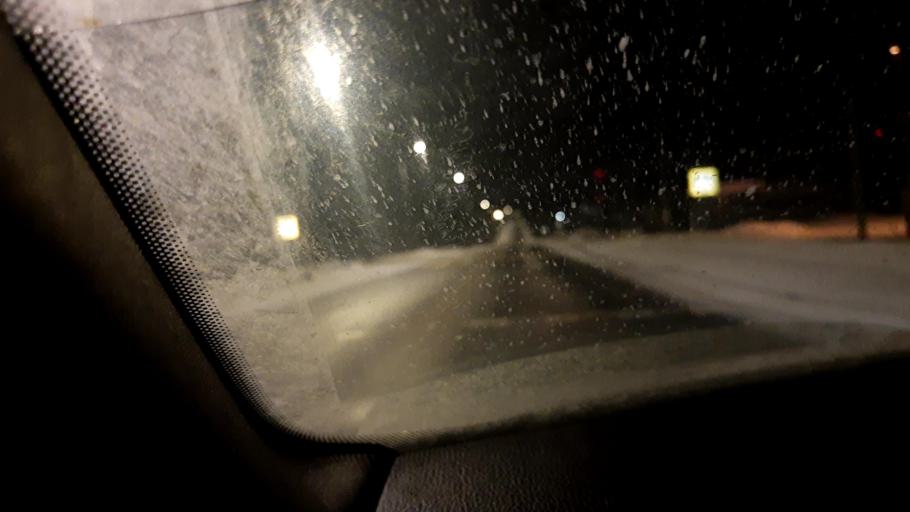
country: RU
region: Moskovskaya
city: Bogorodskoye
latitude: 56.5836
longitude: 38.1506
